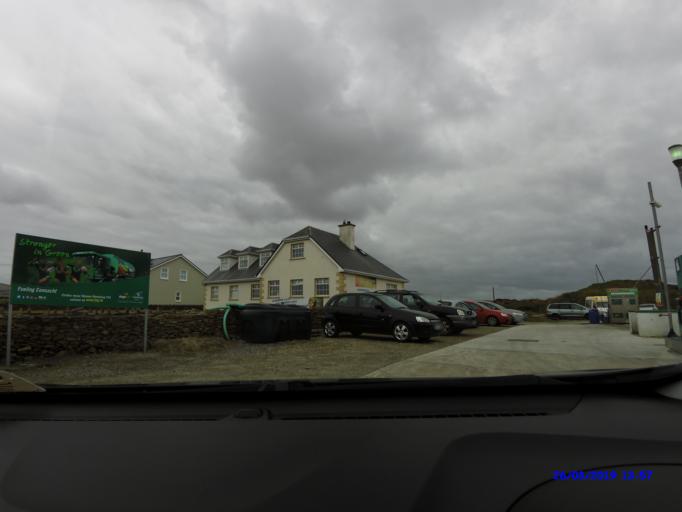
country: IE
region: Connaught
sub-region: Maigh Eo
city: Belmullet
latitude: 54.2079
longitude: -9.9346
